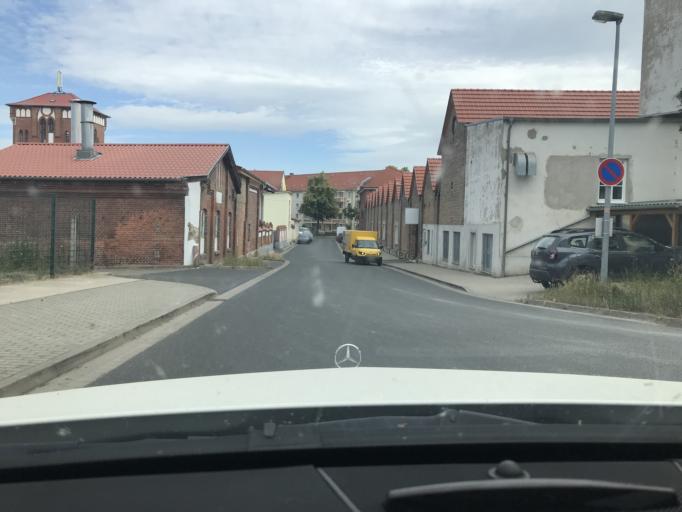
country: DE
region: Thuringia
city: Muehlhausen
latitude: 51.2046
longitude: 10.4763
